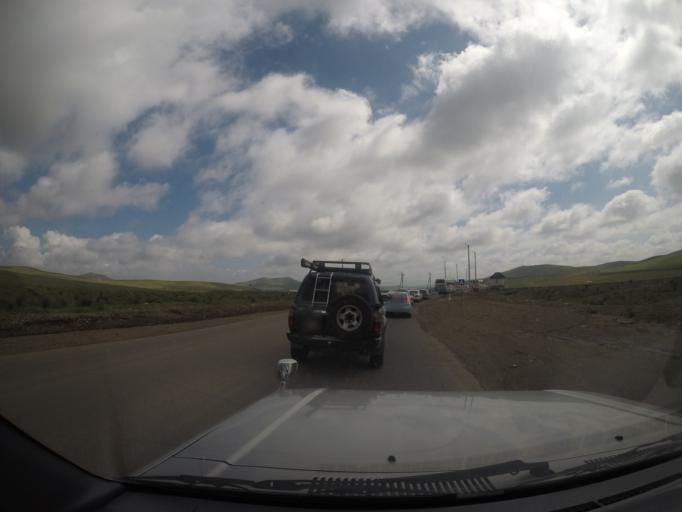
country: MN
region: Central Aimak
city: Dzuunmod
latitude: 47.6872
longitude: 107.1961
